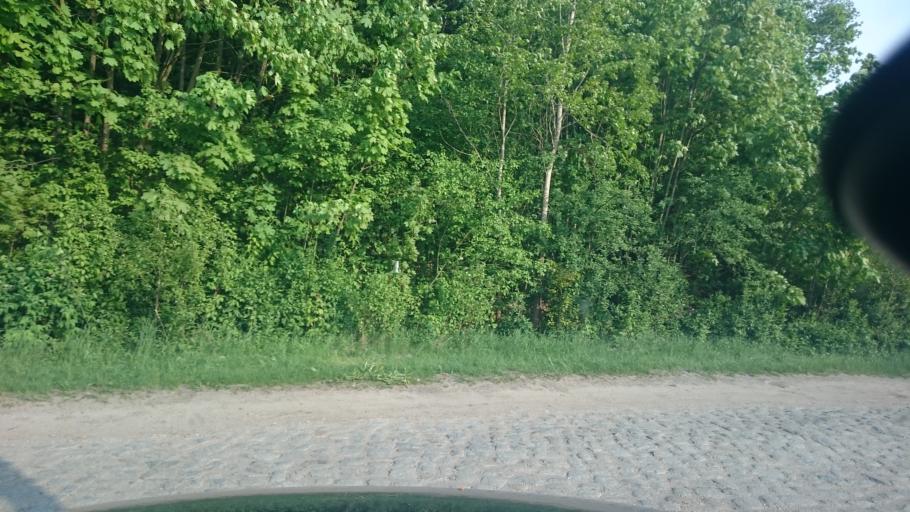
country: PL
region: Kujawsko-Pomorskie
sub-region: Grudziadz
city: Grudziadz
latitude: 53.4792
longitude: 18.8135
